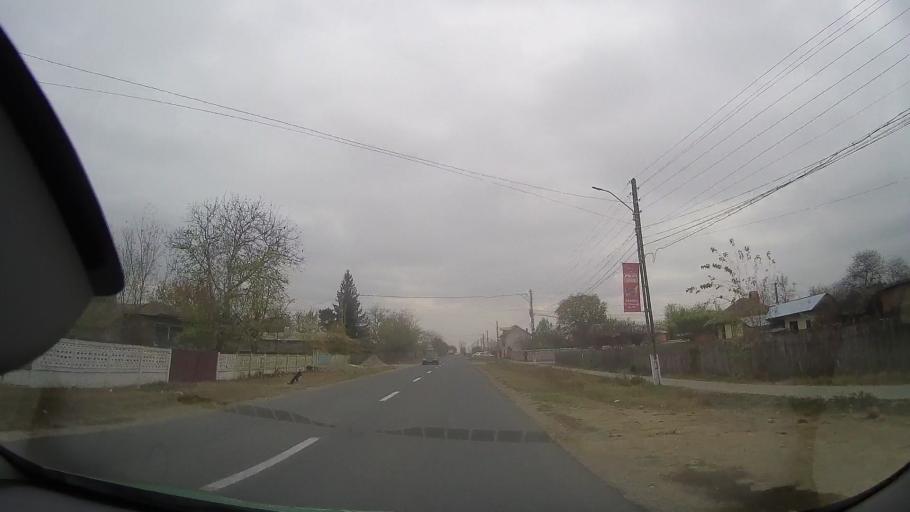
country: RO
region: Ialomita
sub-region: Comuna Garbovi
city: Garbovi
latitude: 44.7815
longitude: 26.7559
